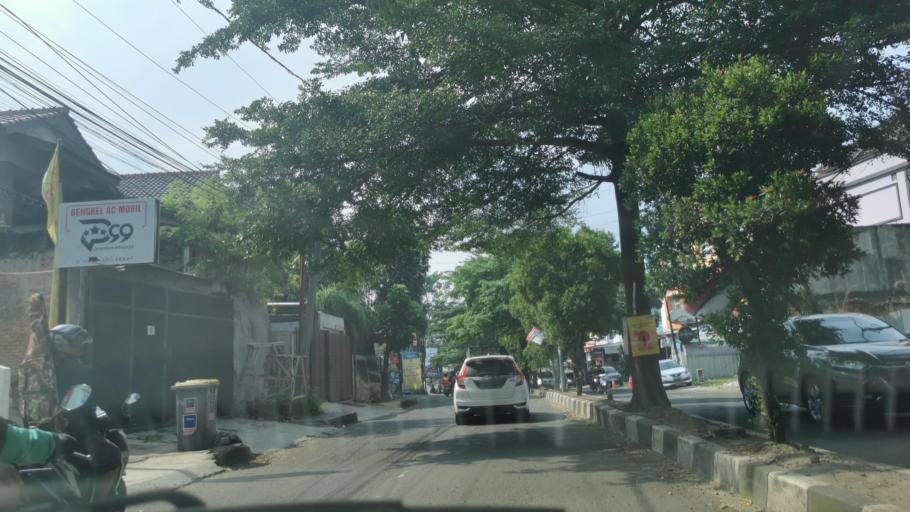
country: ID
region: West Java
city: Depok
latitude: -6.3822
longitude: 106.8417
